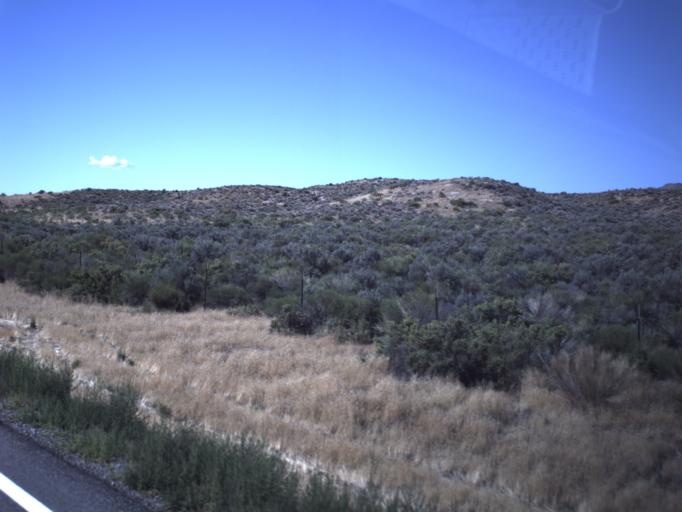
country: US
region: Utah
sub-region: Tooele County
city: Tooele
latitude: 40.1972
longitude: -112.4138
